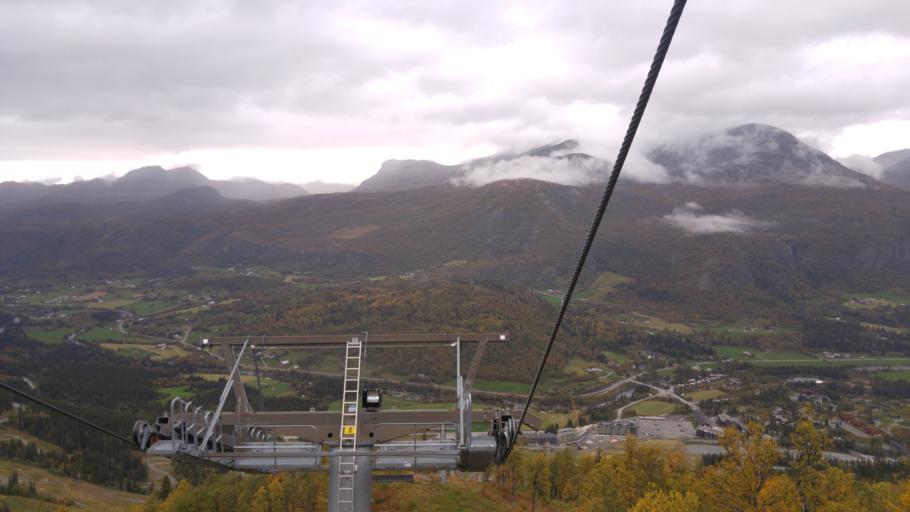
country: NO
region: Buskerud
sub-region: Hemsedal
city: Hemsedal
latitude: 60.8531
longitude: 8.5122
